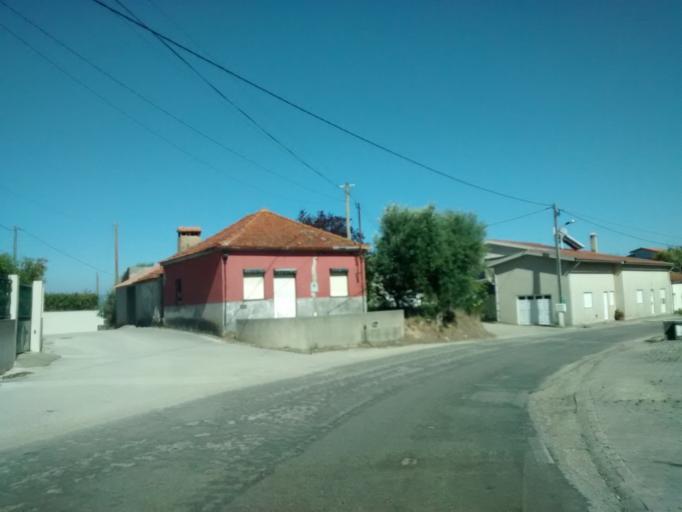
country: PT
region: Aveiro
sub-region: Anadia
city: Sangalhos
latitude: 40.4441
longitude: -8.5034
